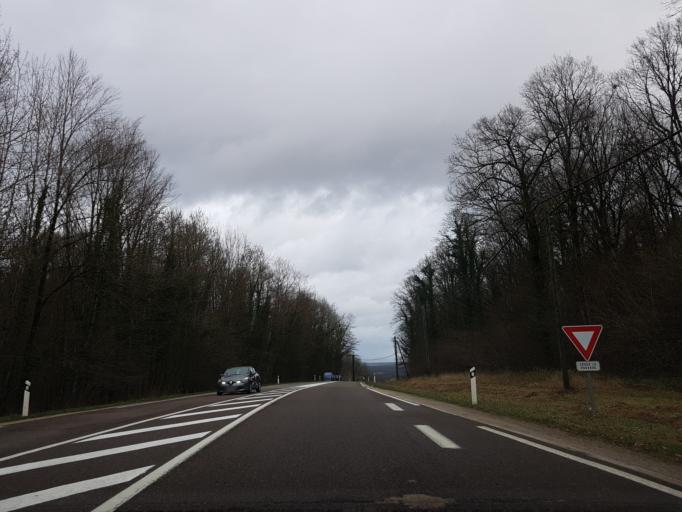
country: FR
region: Franche-Comte
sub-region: Departement de la Haute-Saone
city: Scey-sur-Saone-et-Saint-Albin
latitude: 47.6896
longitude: 6.0054
